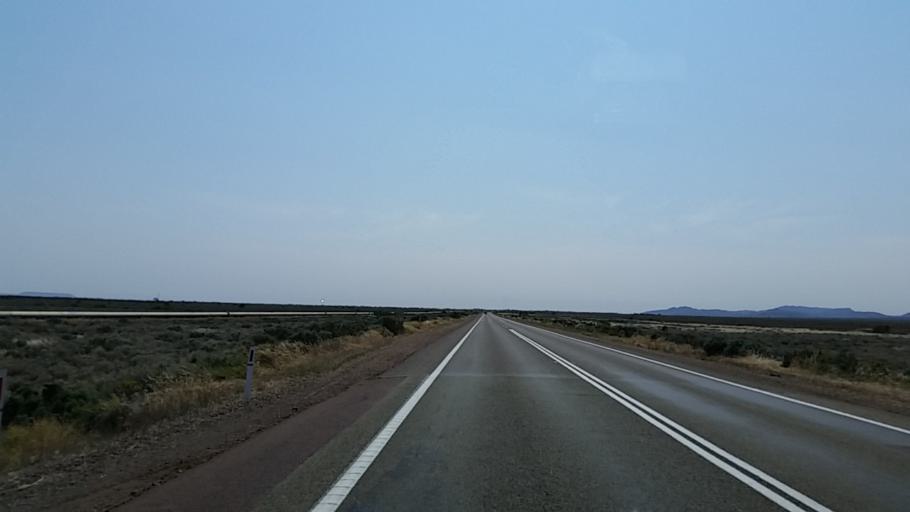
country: AU
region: South Australia
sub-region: Port Augusta
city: Port Augusta
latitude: -32.6729
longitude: 137.9342
